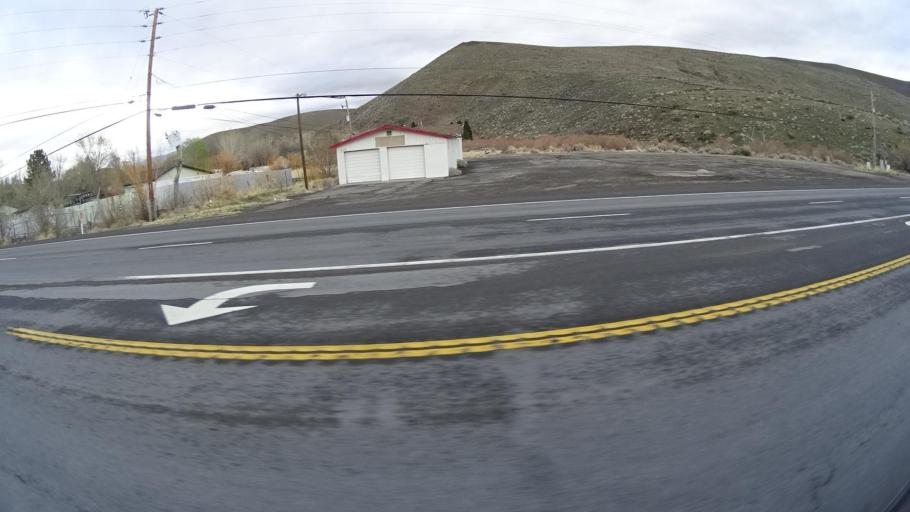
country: US
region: Nevada
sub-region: Storey County
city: Virginia City
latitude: 39.3464
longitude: -119.7789
